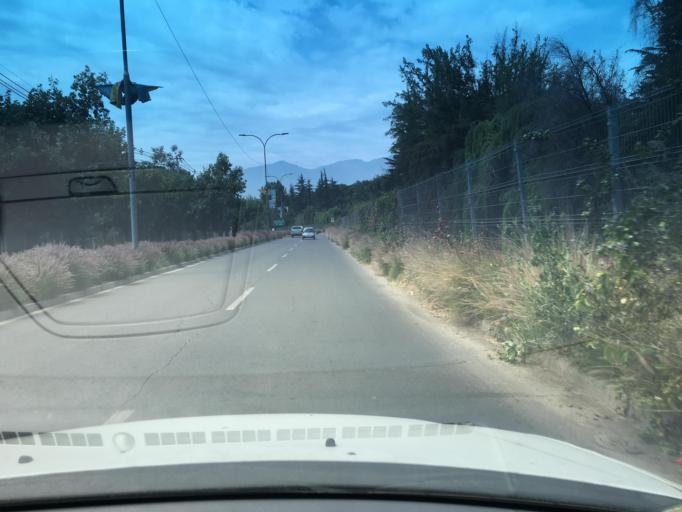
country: CL
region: Santiago Metropolitan
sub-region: Provincia de Santiago
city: Santiago
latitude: -33.3809
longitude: -70.6372
